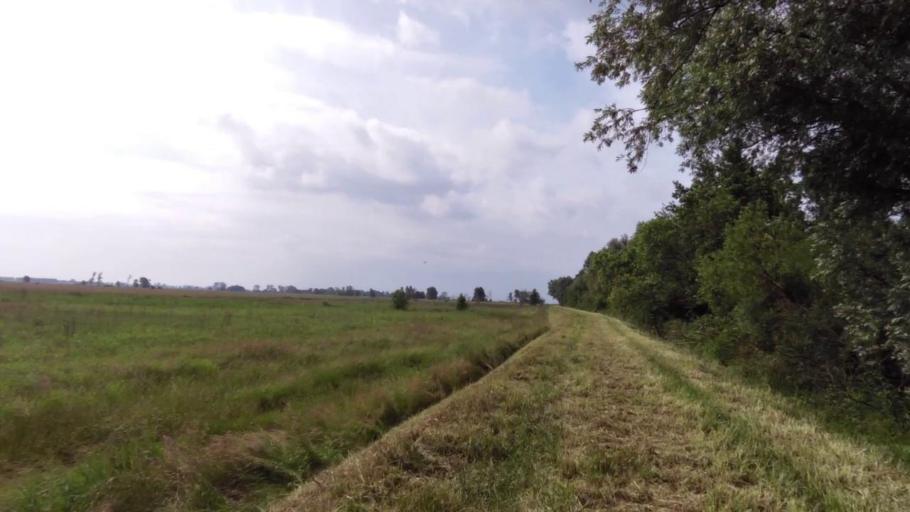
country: PL
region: West Pomeranian Voivodeship
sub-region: Powiat policki
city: Police
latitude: 53.5410
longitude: 14.6782
